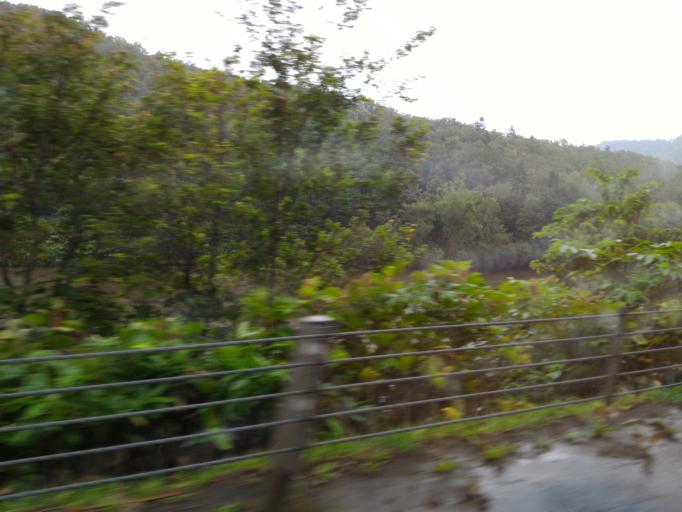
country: JP
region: Hokkaido
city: Nayoro
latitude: 44.7251
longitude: 142.1672
